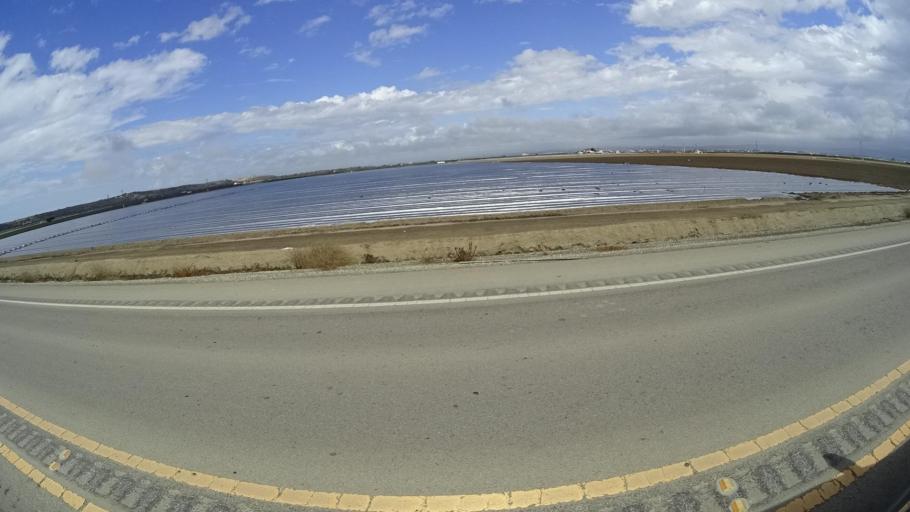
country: US
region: California
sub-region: Monterey County
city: Marina
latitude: 36.6786
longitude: -121.7382
